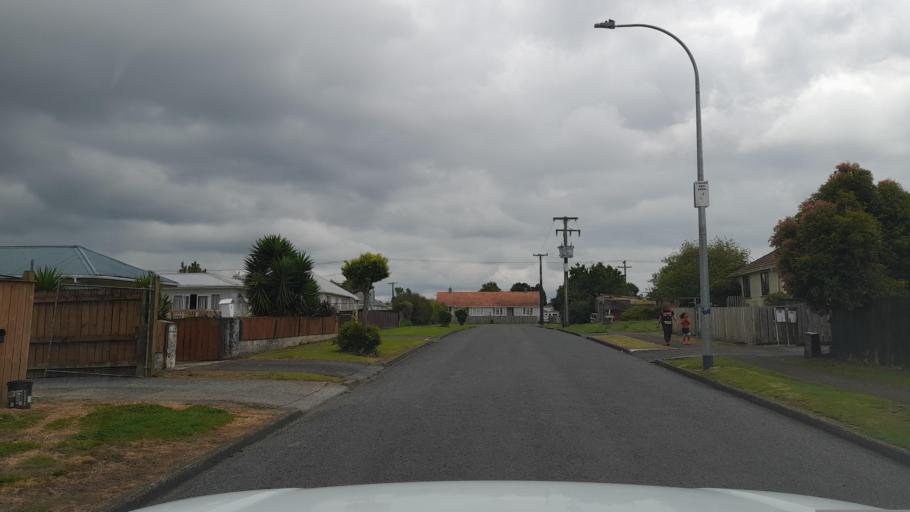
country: NZ
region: Northland
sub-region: Far North District
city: Waimate North
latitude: -35.4069
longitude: 173.8066
